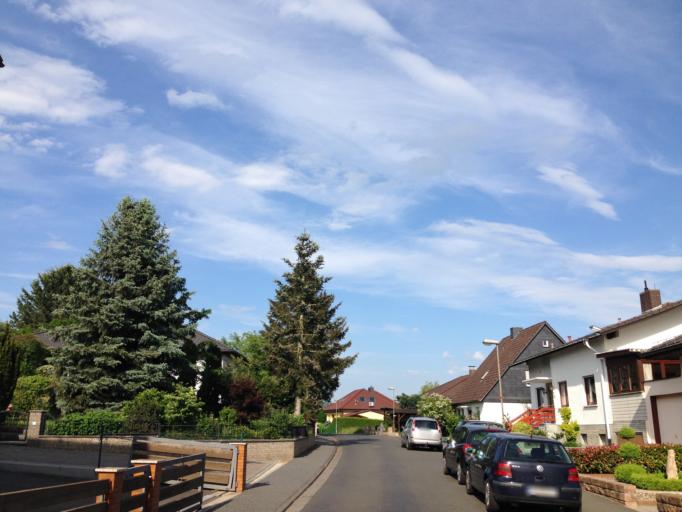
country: DE
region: Hesse
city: Staufenberg
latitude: 50.6608
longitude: 8.7377
